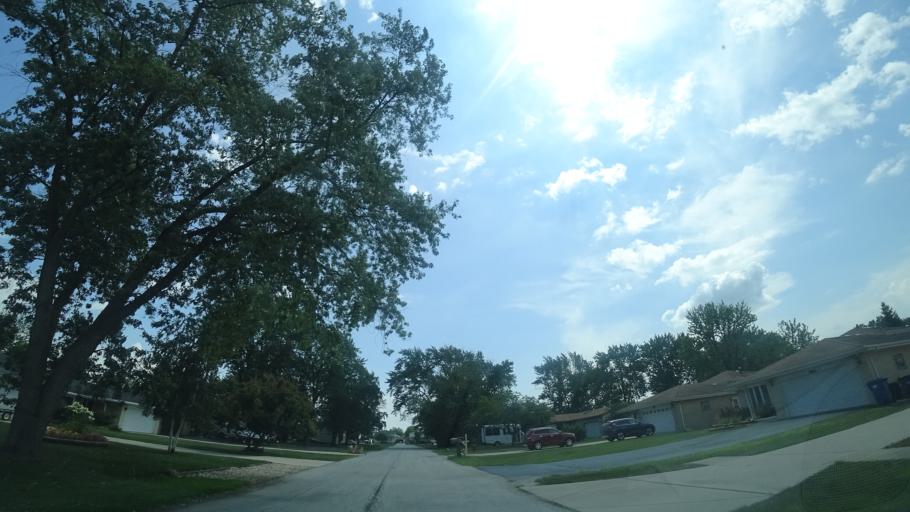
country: US
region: Illinois
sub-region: Cook County
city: Alsip
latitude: 41.6749
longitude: -87.7456
